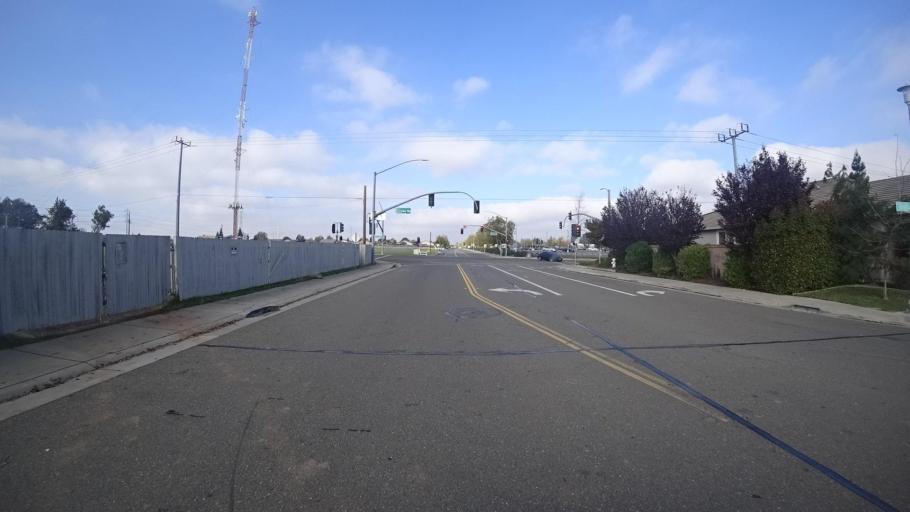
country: US
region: California
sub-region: Sacramento County
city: Vineyard
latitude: 38.4522
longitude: -121.3487
